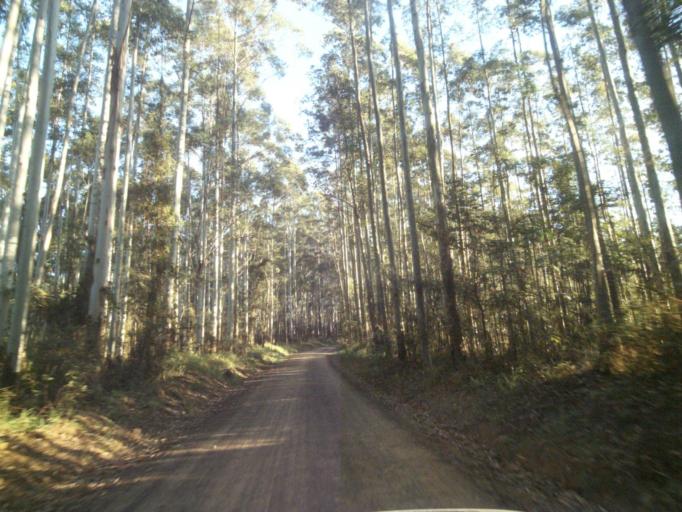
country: BR
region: Parana
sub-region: Telemaco Borba
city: Telemaco Borba
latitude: -24.5088
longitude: -50.6023
